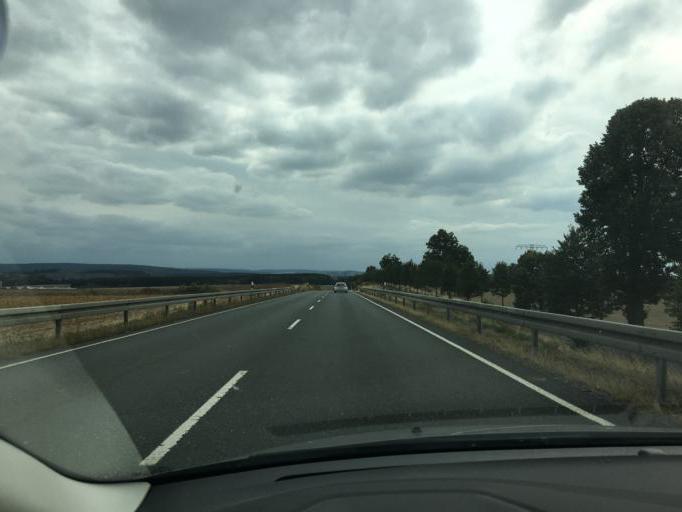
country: DE
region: Thuringia
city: Bad Lobenstein
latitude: 50.4700
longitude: 11.6428
